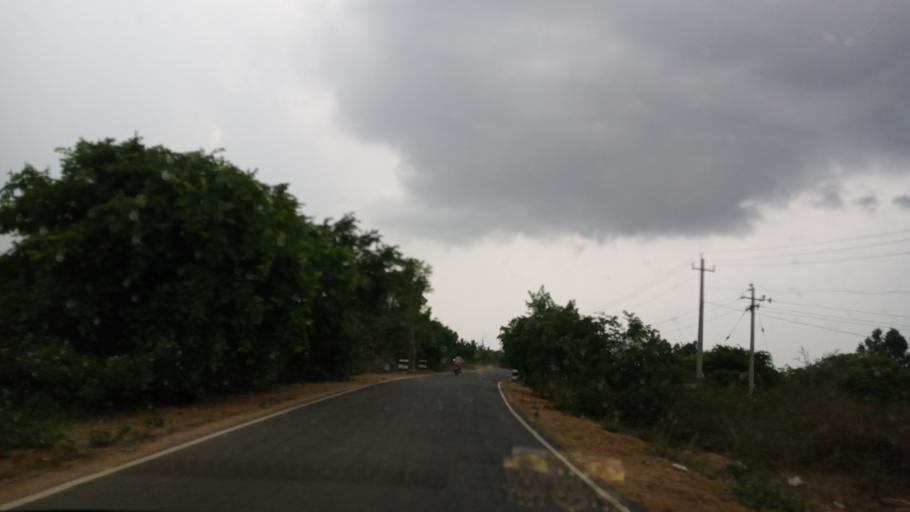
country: IN
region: Karnataka
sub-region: Kolar
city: Mulbagal
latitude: 13.1294
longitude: 78.3535
